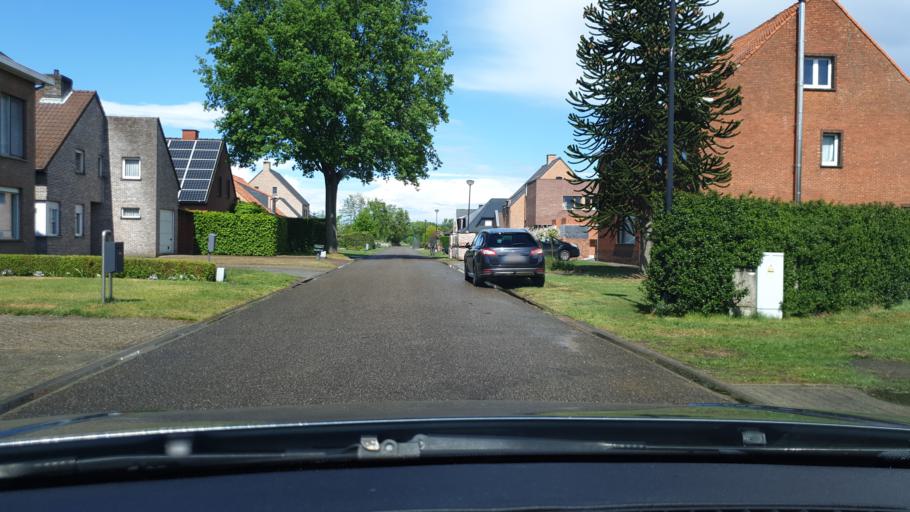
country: BE
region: Flanders
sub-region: Provincie Antwerpen
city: Geel
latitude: 51.1868
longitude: 4.9852
